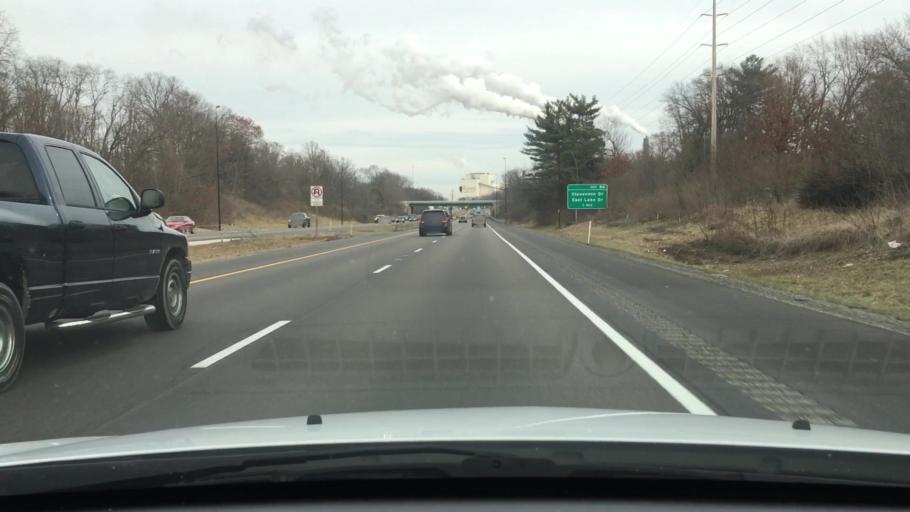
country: US
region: Illinois
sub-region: Sangamon County
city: Southern View
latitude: 39.7479
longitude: -89.6199
